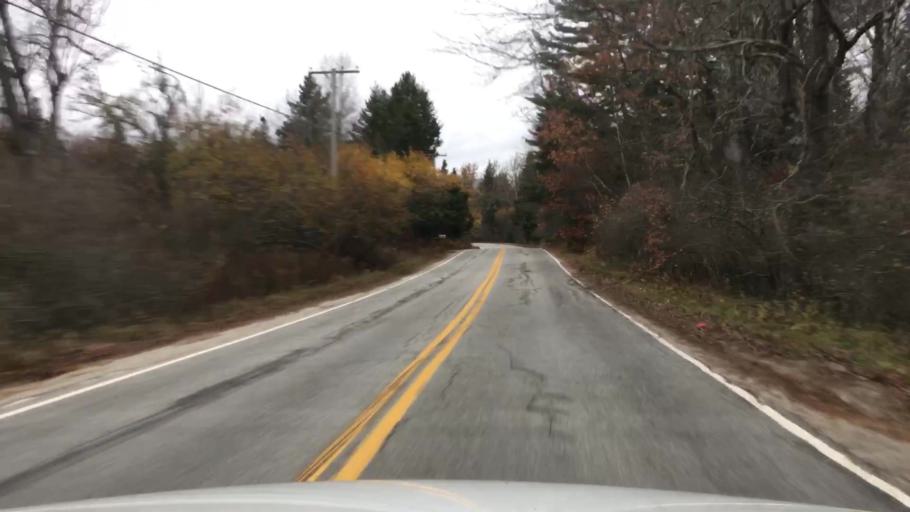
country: US
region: Maine
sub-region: Hancock County
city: Sedgwick
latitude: 44.2899
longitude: -68.5551
